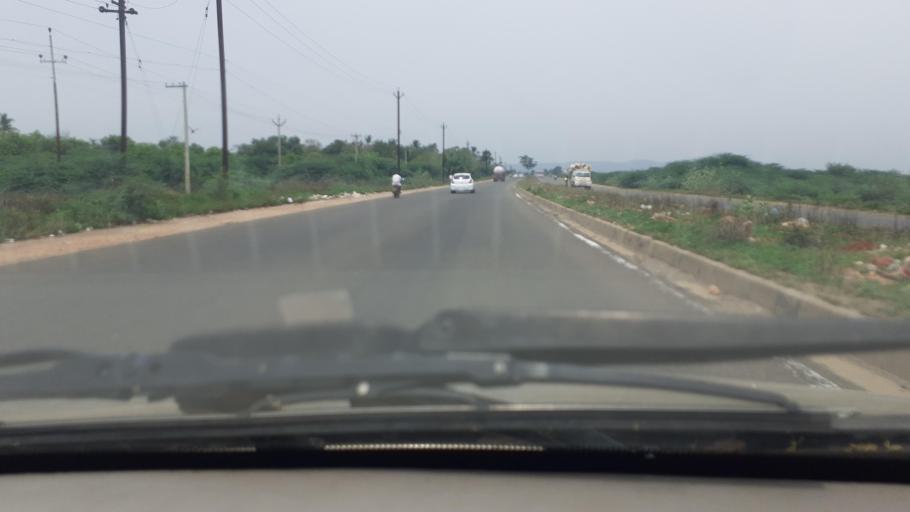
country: IN
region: Tamil Nadu
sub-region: Tirunelveli Kattabo
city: Tirunelveli
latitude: 8.7133
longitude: 77.7939
